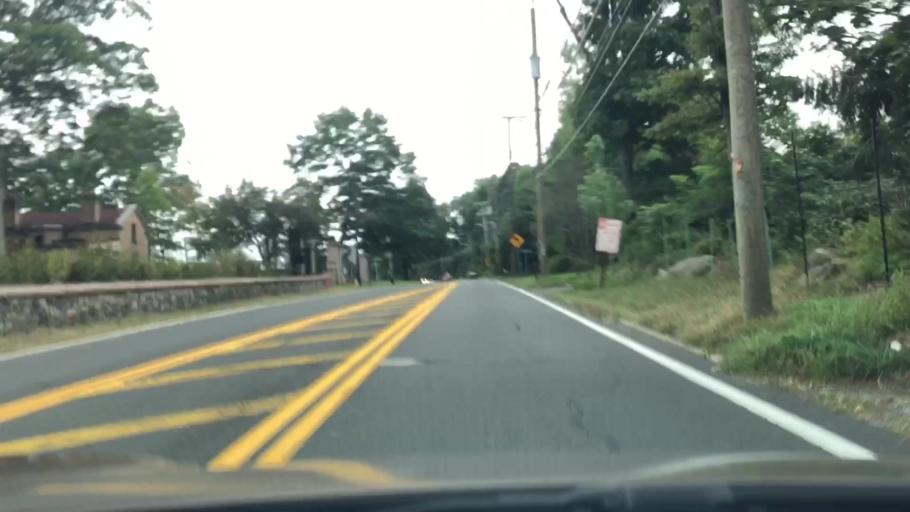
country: US
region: New York
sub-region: Westchester County
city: Ossining
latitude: 41.1245
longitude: -73.8618
